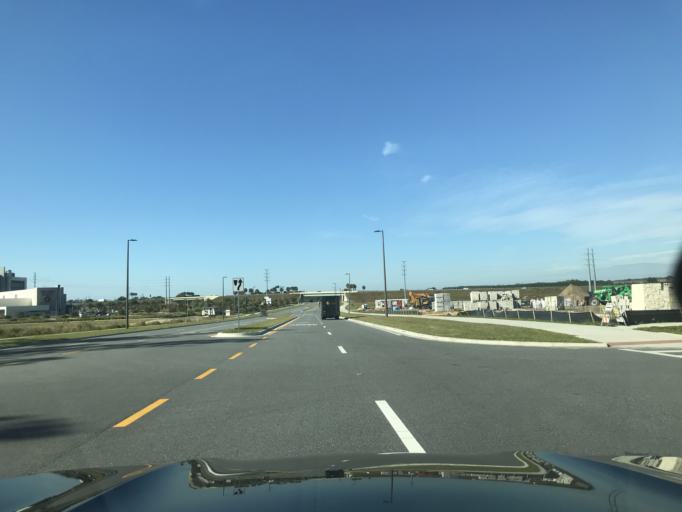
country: US
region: Florida
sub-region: Orange County
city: Oakland
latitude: 28.4598
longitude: -81.6305
